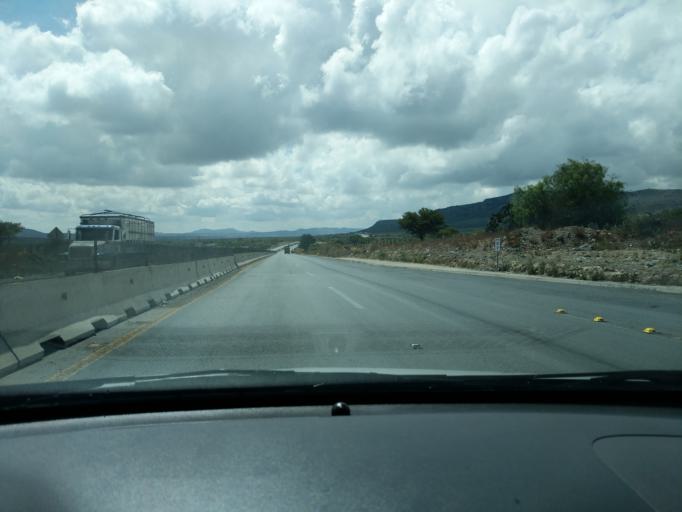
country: MX
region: Zacatecas
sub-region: Pinos
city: Santiago
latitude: 22.4074
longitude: -101.3969
